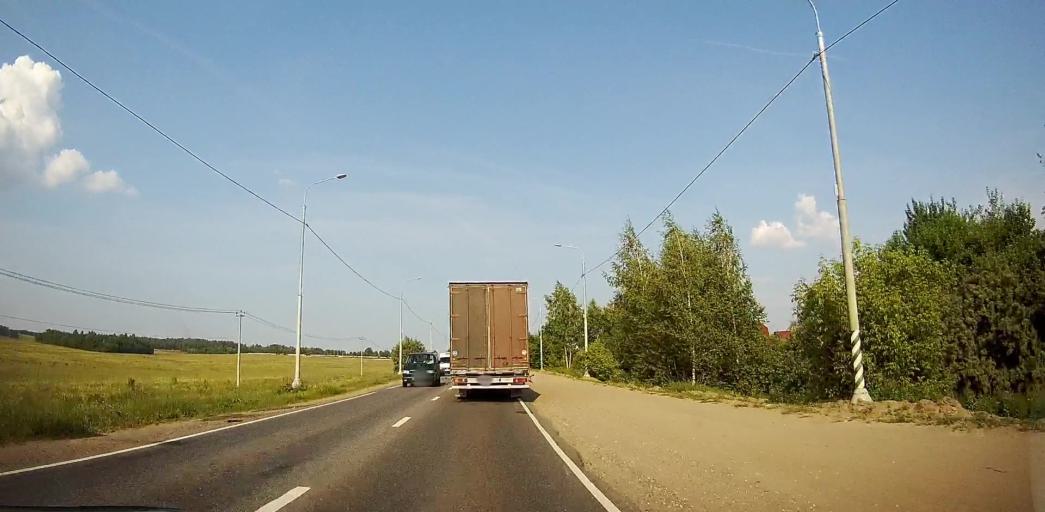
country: RU
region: Moskovskaya
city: Ostrovtsy
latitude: 55.5388
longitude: 38.0289
